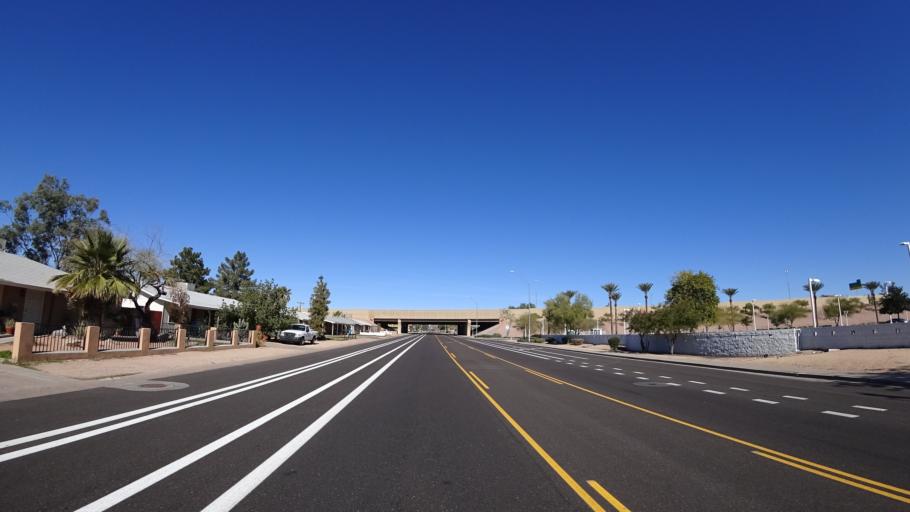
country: US
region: Arizona
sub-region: Maricopa County
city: Tempe Junction
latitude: 33.4555
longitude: -111.9785
